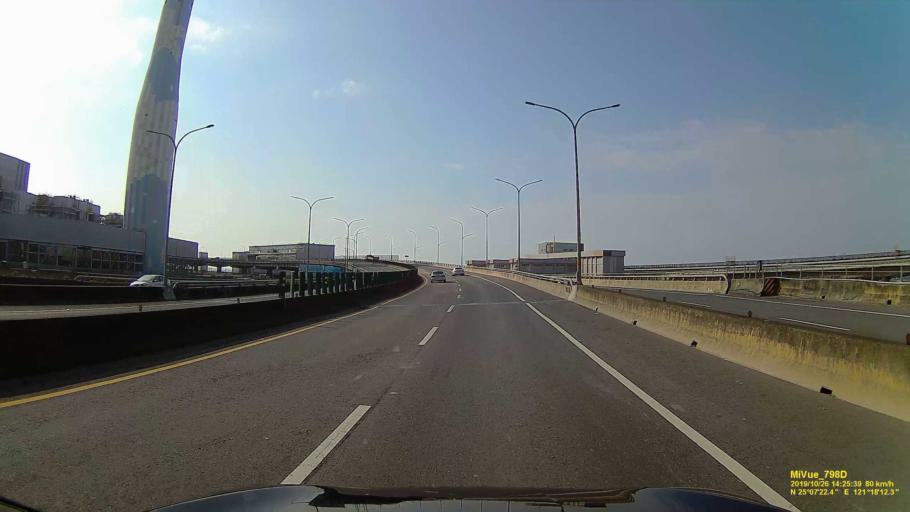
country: TW
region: Taiwan
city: Taoyuan City
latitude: 25.1228
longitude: 121.3033
